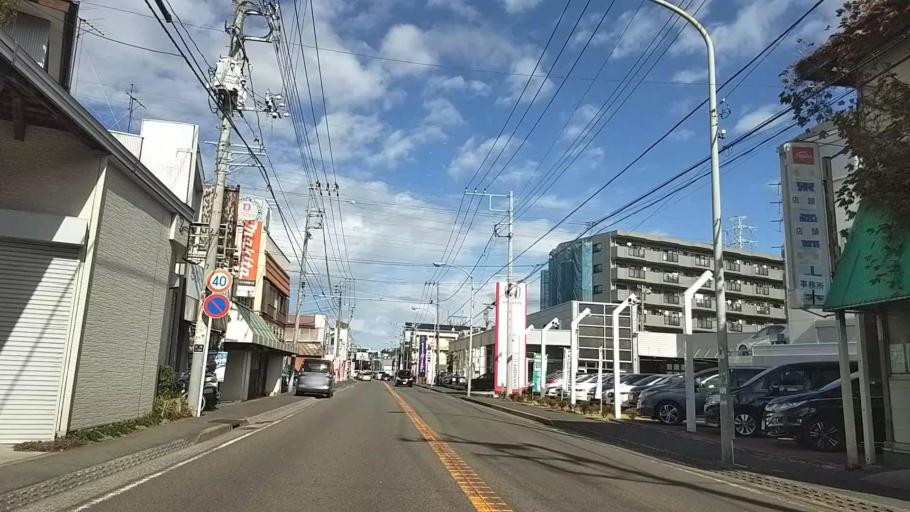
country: JP
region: Kanagawa
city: Yokohama
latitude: 35.5283
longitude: 139.6337
